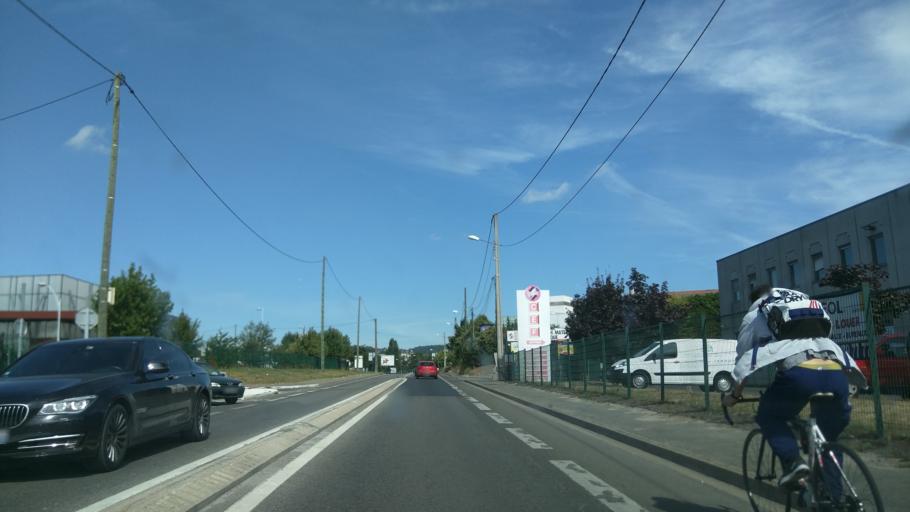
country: FR
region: Ile-de-France
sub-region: Departement des Yvelines
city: Sartrouville
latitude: 48.9547
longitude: 2.2055
